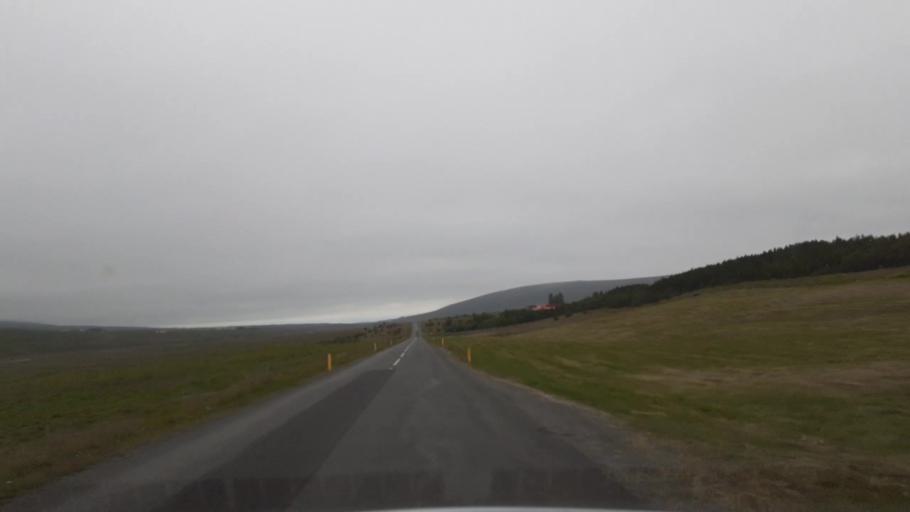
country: IS
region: Northeast
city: Siglufjoerdur
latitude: 65.7336
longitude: -19.1164
